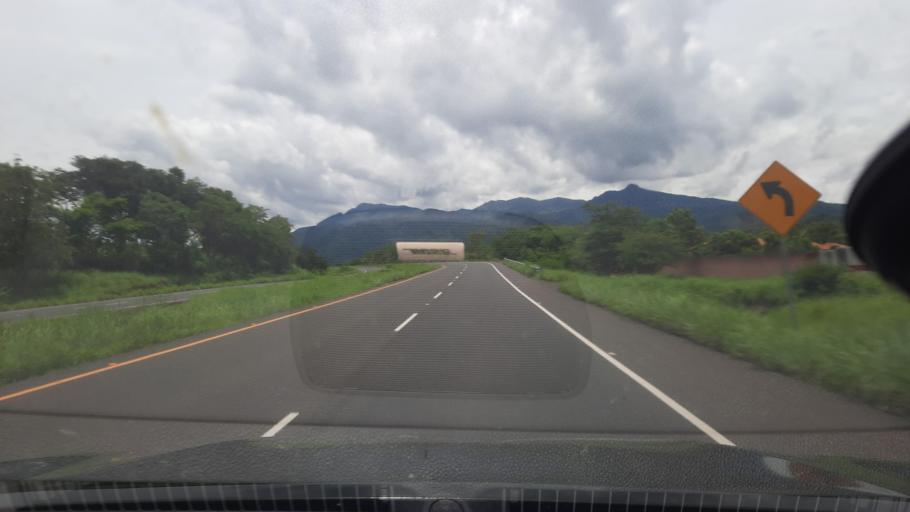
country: HN
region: Valle
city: Aramecina
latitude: 13.7688
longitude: -87.7039
